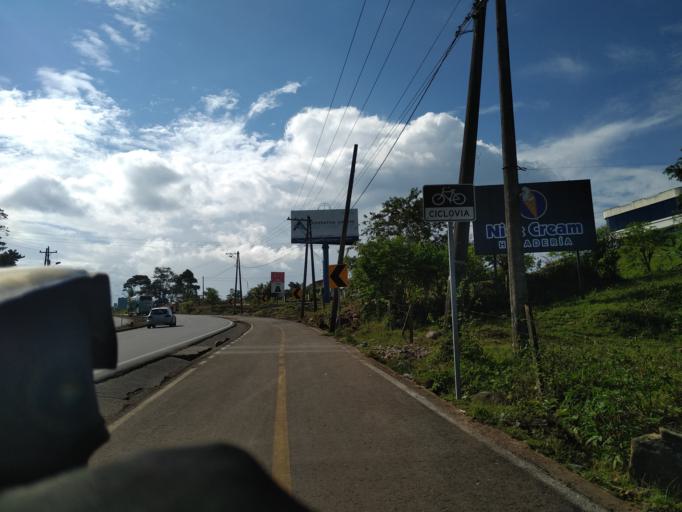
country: EC
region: Napo
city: Tena
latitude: -1.0347
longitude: -77.7981
